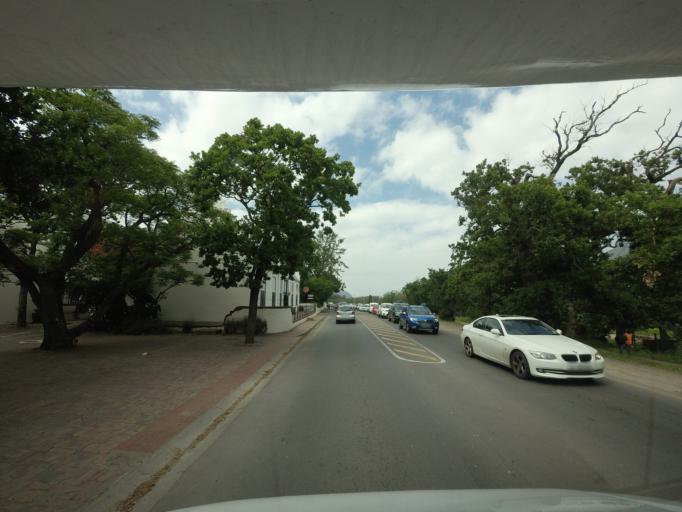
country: ZA
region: Western Cape
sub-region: City of Cape Town
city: Constantia
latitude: -34.0321
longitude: 18.3564
